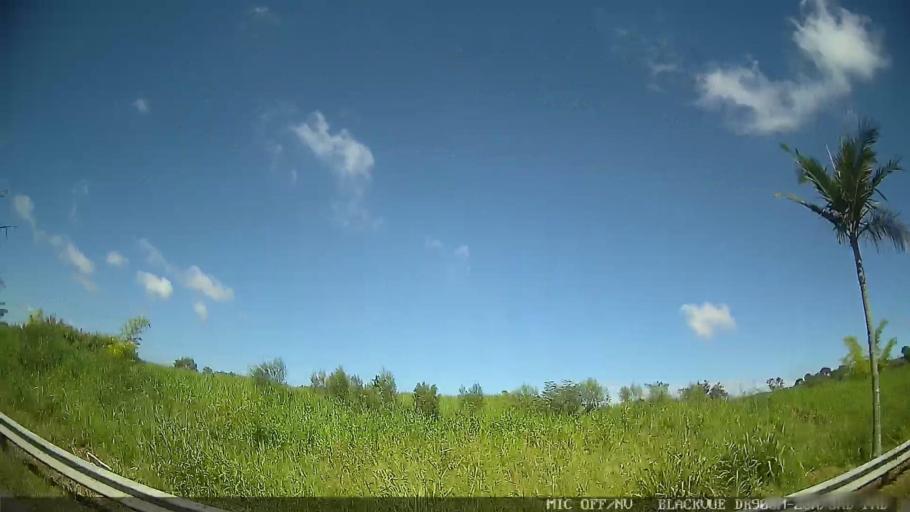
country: BR
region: Sao Paulo
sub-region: Suzano
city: Suzano
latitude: -23.5612
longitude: -46.2563
